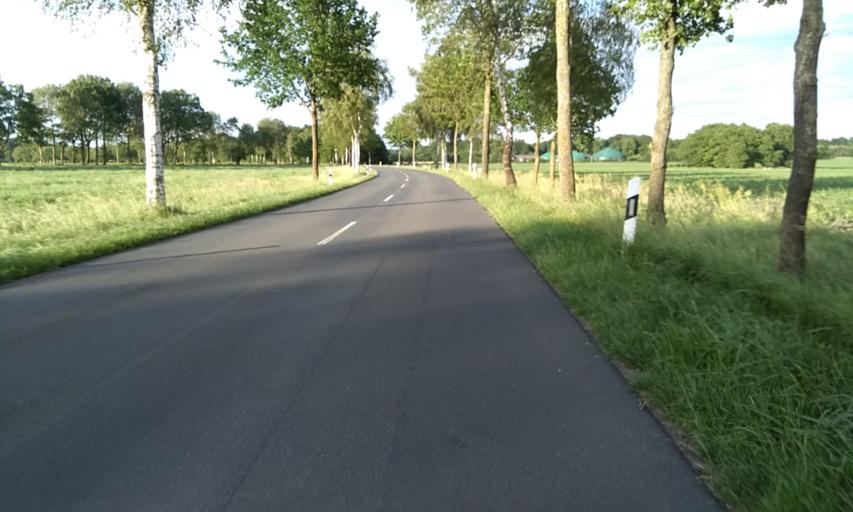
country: DE
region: Lower Saxony
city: Anderlingen
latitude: 53.3862
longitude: 9.3165
